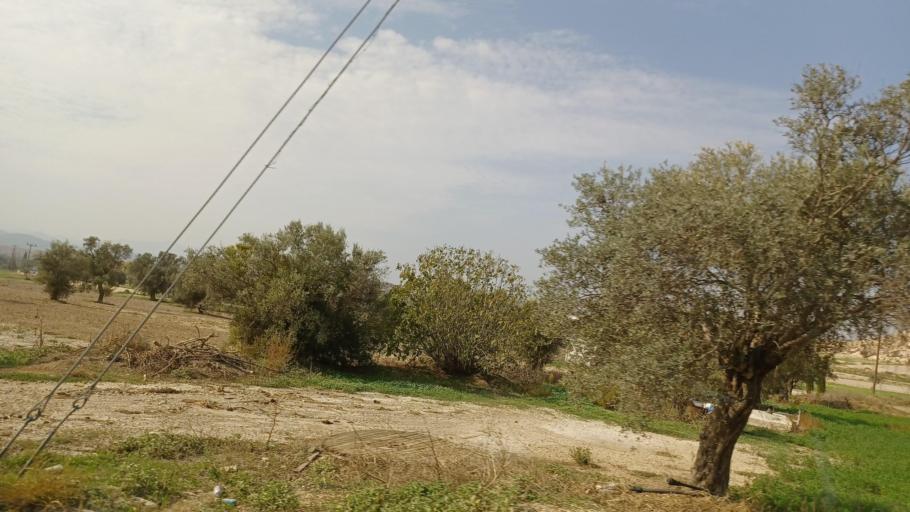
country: CY
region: Lefkosia
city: Lympia
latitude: 34.9881
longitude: 33.4552
